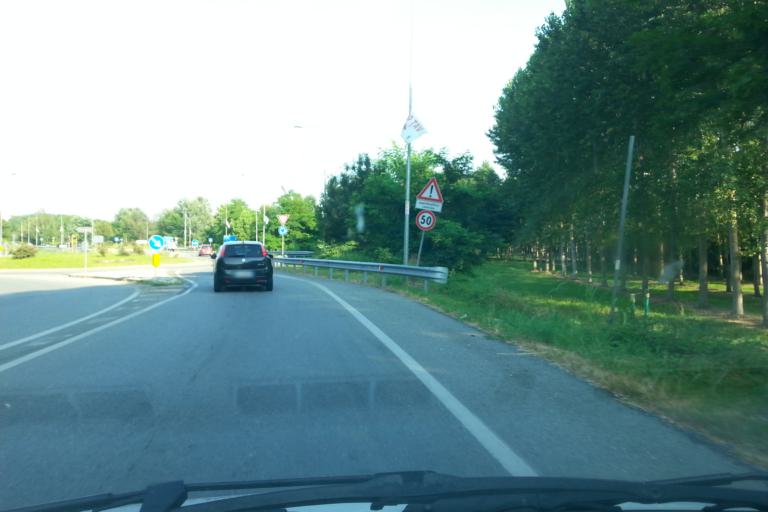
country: IT
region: Piedmont
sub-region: Provincia di Torino
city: Sant'Ambrogio di Torino
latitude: 45.1039
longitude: 7.3723
